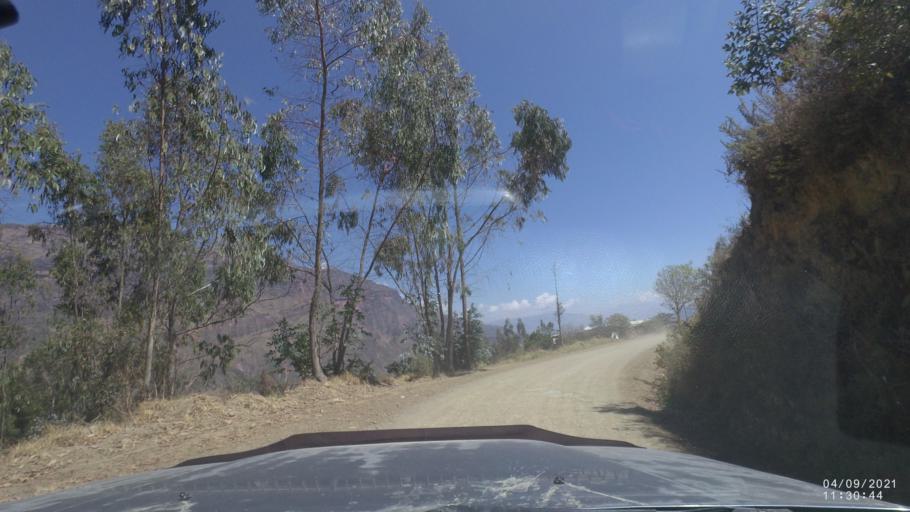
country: BO
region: Cochabamba
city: Colchani
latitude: -17.2357
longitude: -66.5202
